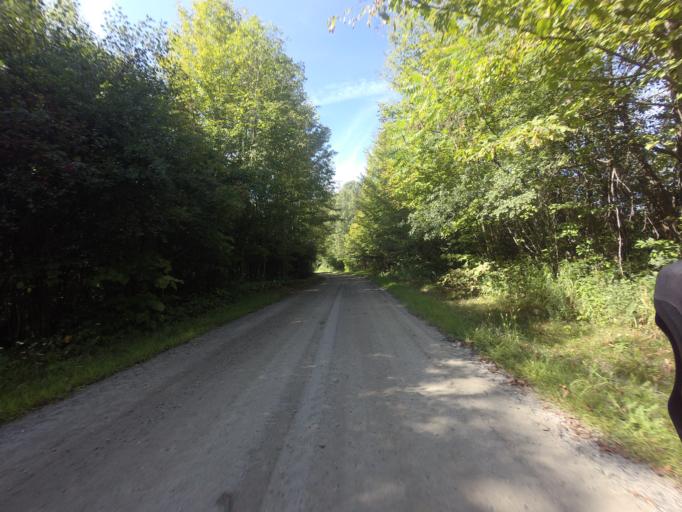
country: CA
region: Ontario
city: Perth
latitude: 44.9380
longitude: -76.3771
